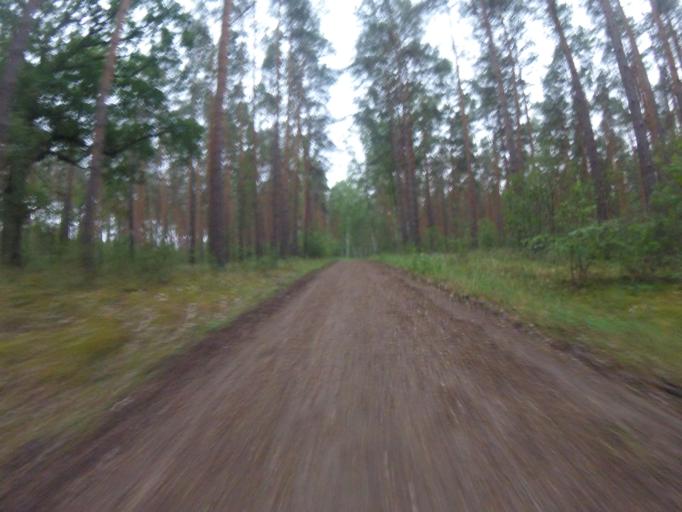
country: DE
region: Brandenburg
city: Gross Koris
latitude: 52.2067
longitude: 13.6986
